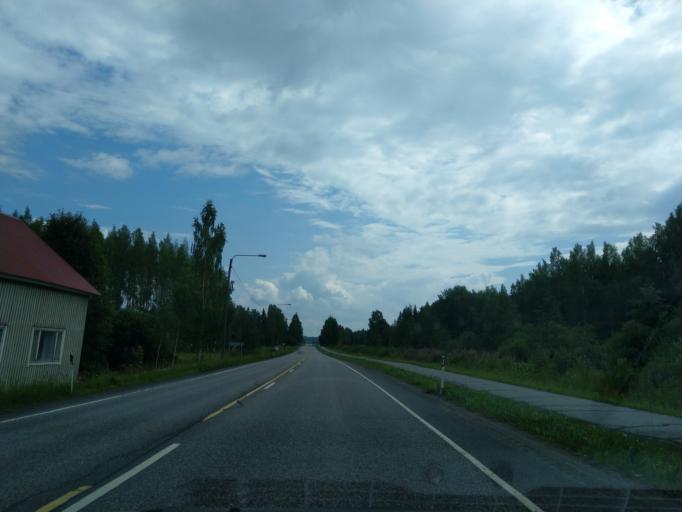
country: FI
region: South Karelia
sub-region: Imatra
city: Parikkala
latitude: 61.5940
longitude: 29.4856
